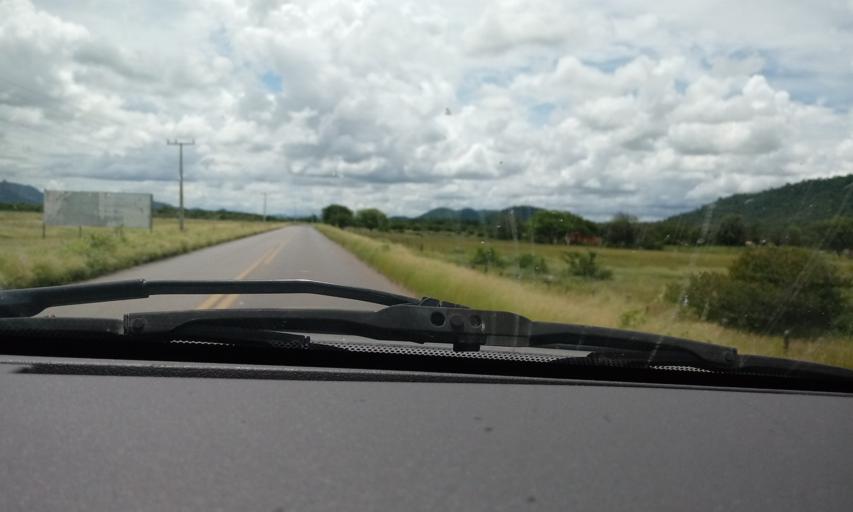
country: BR
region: Bahia
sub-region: Guanambi
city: Guanambi
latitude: -14.1884
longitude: -42.7984
